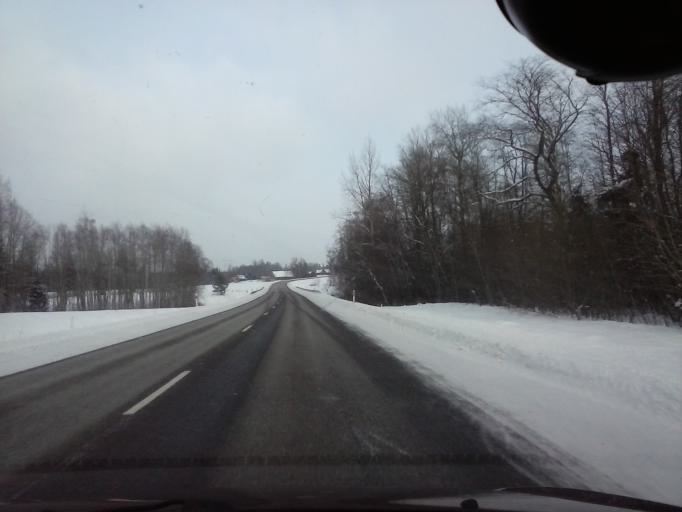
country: EE
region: Paernumaa
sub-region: Saarde vald
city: Kilingi-Nomme
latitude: 58.1720
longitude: 25.0315
